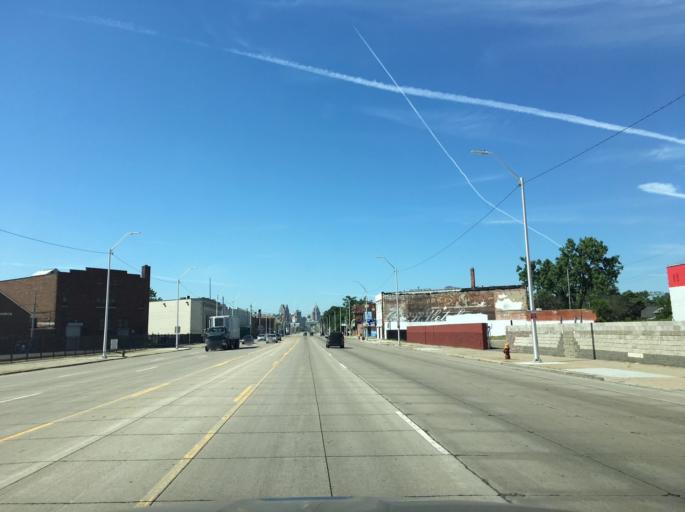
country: US
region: Michigan
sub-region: Wayne County
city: Detroit
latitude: 42.3607
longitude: -83.0267
